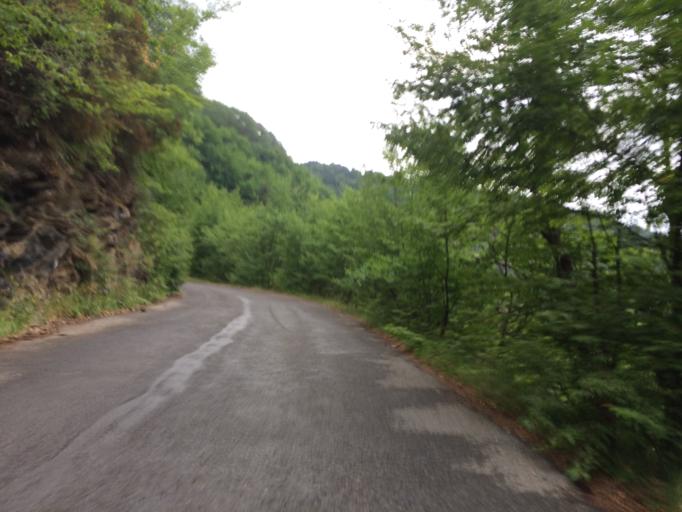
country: IT
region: Liguria
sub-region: Provincia di Imperia
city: Triora
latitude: 43.9778
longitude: 7.7466
